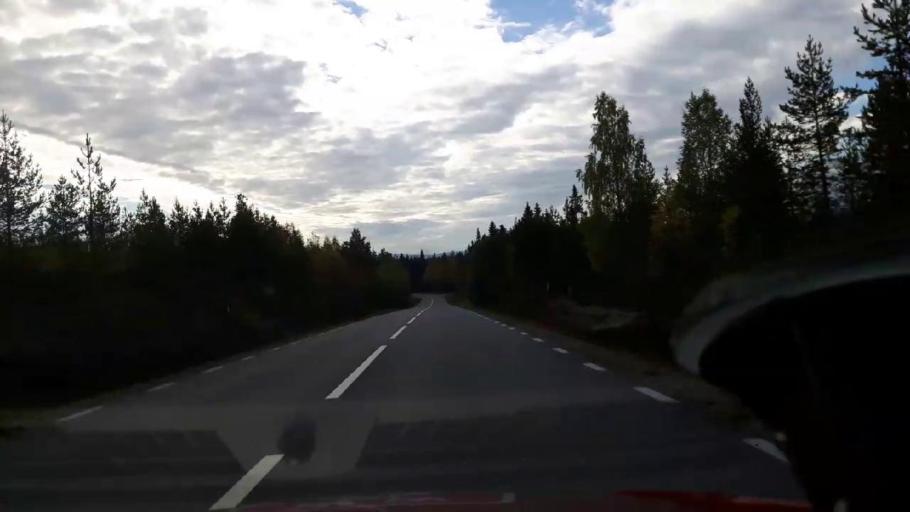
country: SE
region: Gaevleborg
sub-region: Ljusdals Kommun
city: Farila
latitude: 61.9995
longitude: 15.2412
